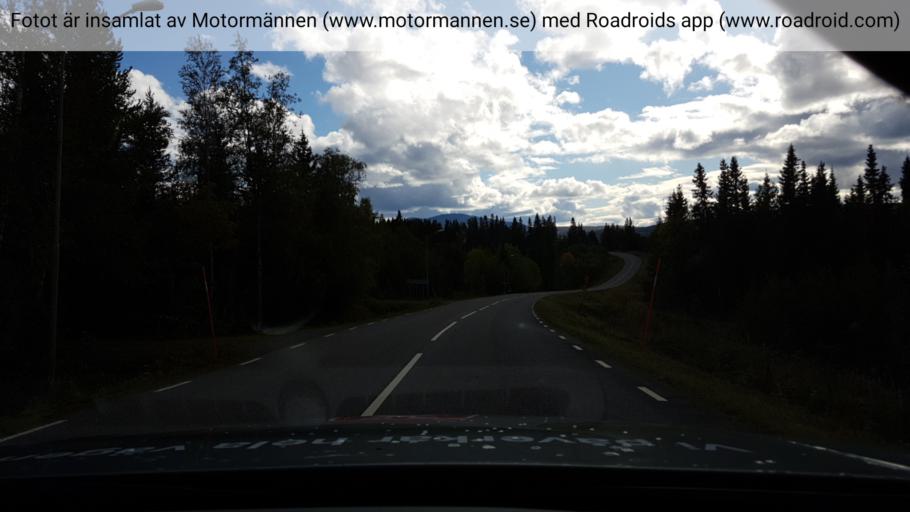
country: SE
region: Jaemtland
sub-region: Are Kommun
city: Are
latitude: 63.5646
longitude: 13.0255
